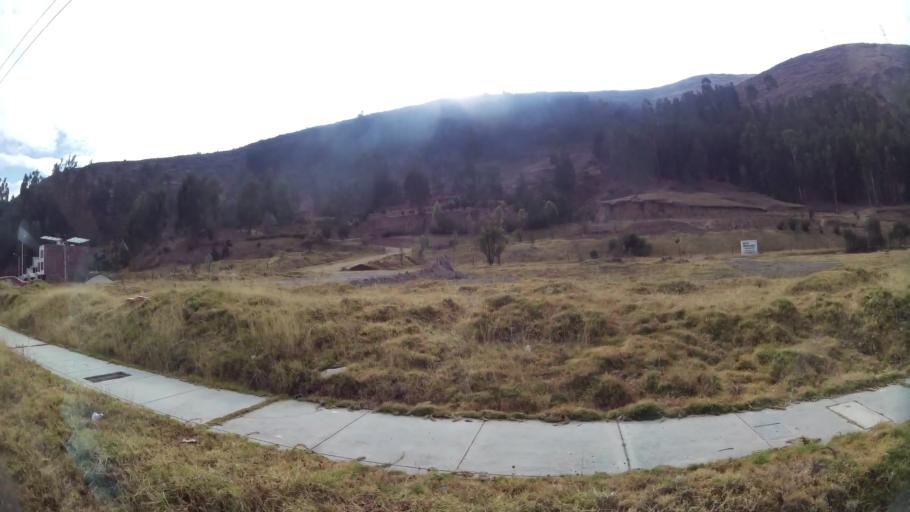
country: PE
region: Junin
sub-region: Provincia de Huancayo
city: Huancayo
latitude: -12.0467
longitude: -75.1868
